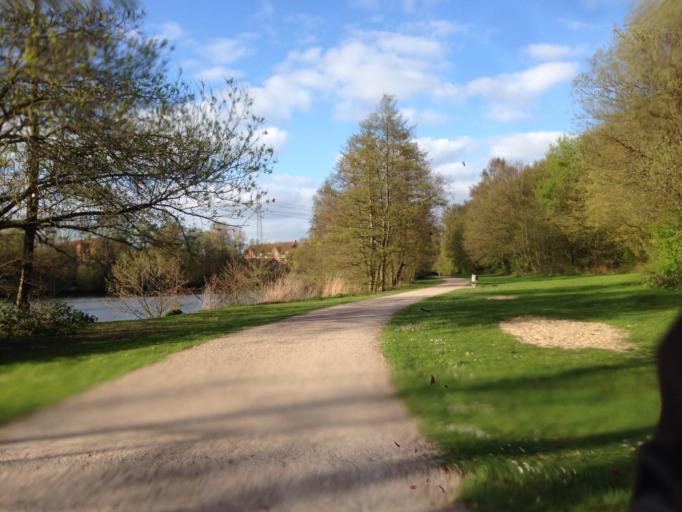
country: DE
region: Hamburg
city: Wandsbek
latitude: 53.5757
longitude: 10.1206
